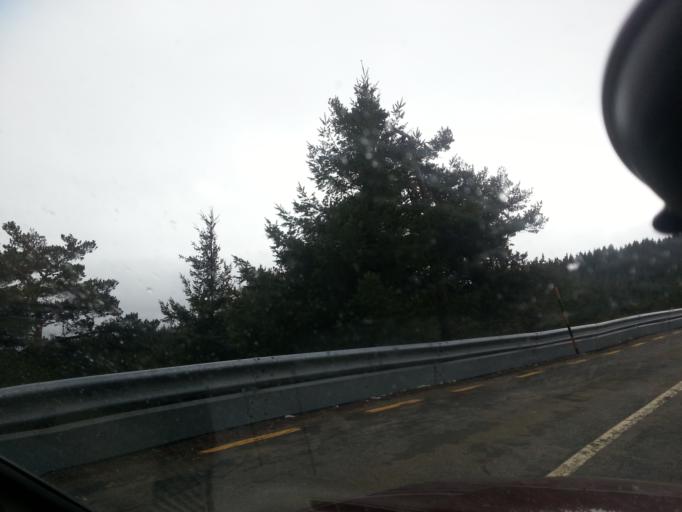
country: PT
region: Guarda
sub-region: Manteigas
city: Manteigas
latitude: 40.4147
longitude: -7.5584
